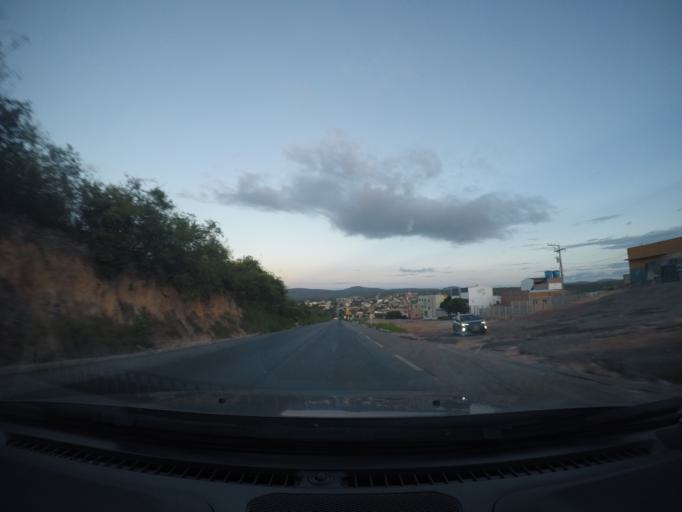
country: BR
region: Bahia
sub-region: Seabra
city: Seabra
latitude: -12.4291
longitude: -41.7847
